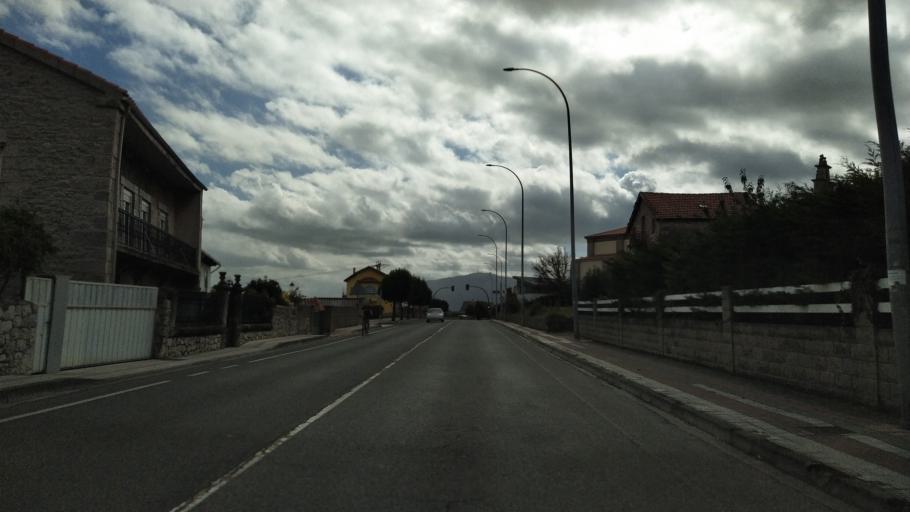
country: ES
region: Cantabria
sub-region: Provincia de Cantabria
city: Camargo
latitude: 43.4252
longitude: -3.8554
